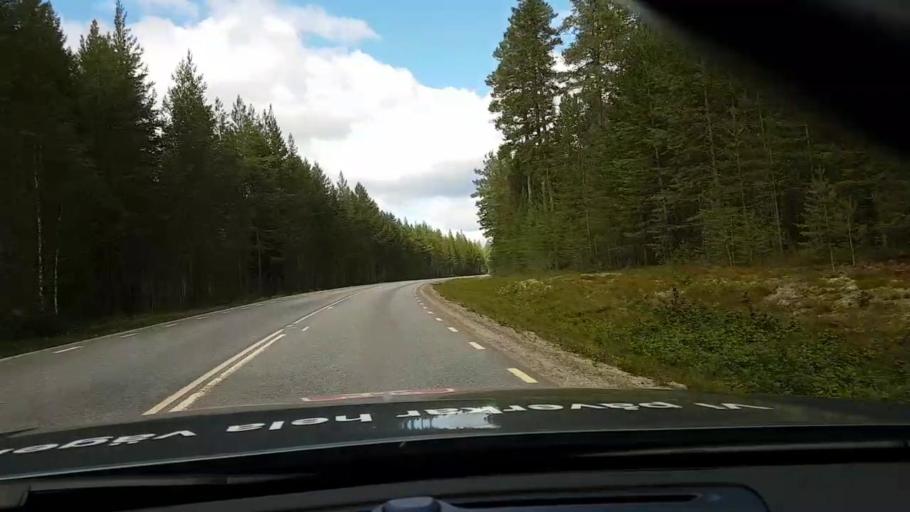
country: SE
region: Vaesternorrland
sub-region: OErnskoeldsviks Kommun
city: Bredbyn
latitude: 63.5322
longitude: 17.9681
